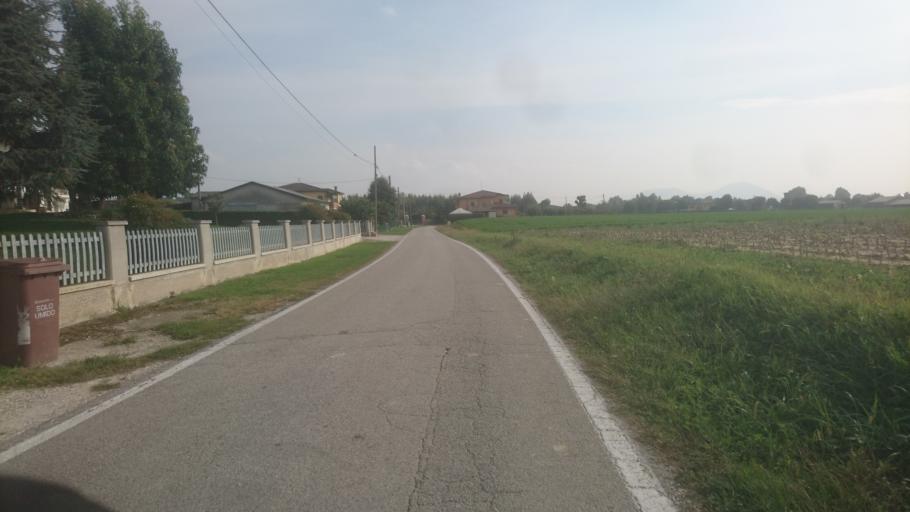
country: IT
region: Veneto
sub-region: Provincia di Vicenza
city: Montegalda
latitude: 45.4610
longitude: 11.6556
